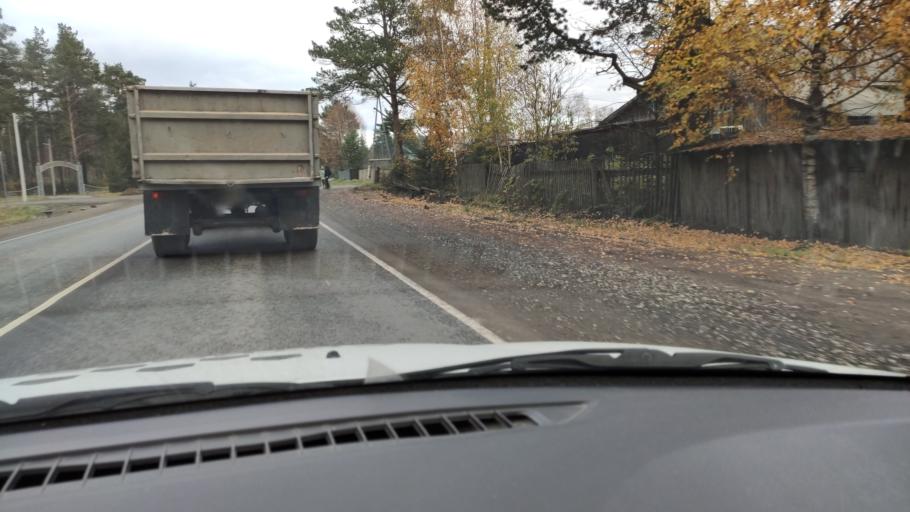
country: RU
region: Kirov
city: Belaya Kholunitsa
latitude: 58.8520
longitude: 50.8312
